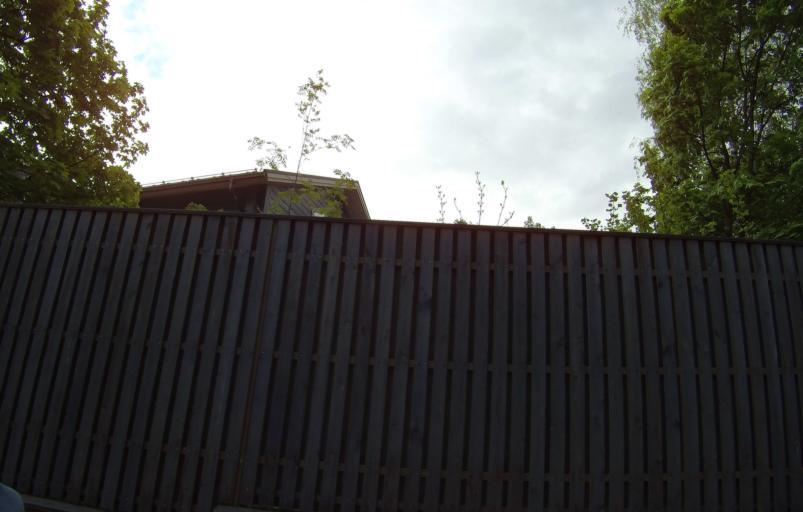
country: RU
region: Moskovskaya
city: Kratovo
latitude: 55.5825
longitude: 38.1678
